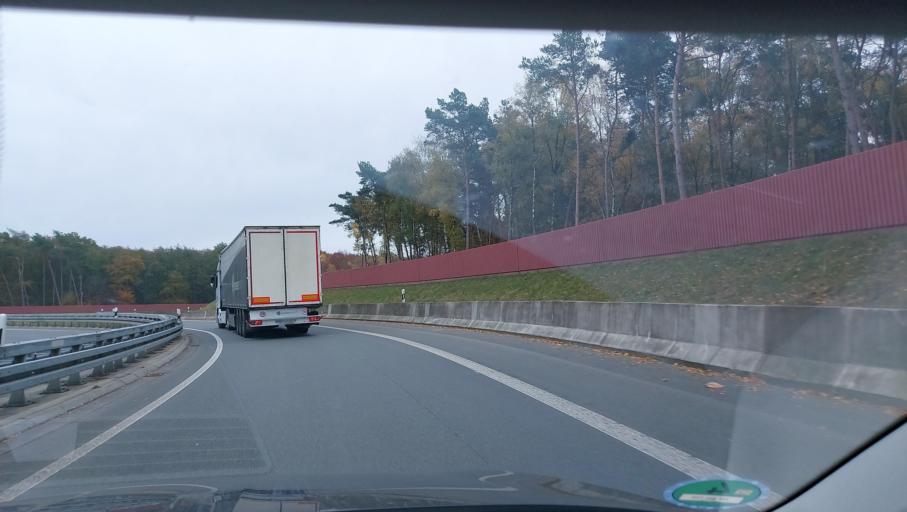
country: DE
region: North Rhine-Westphalia
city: Halle
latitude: 52.0415
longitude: 8.3382
